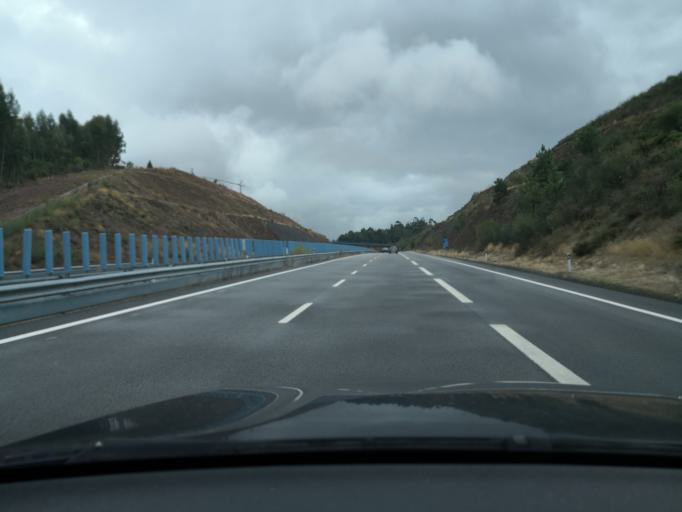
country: PT
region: Porto
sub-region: Lousada
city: Lousada
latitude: 41.2931
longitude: -8.2918
